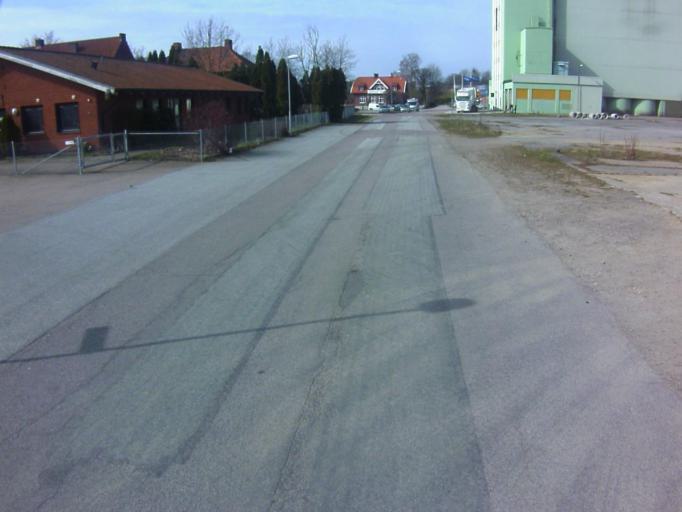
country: SE
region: Skane
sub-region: Kavlinge Kommun
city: Kaevlinge
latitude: 55.7923
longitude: 13.1159
